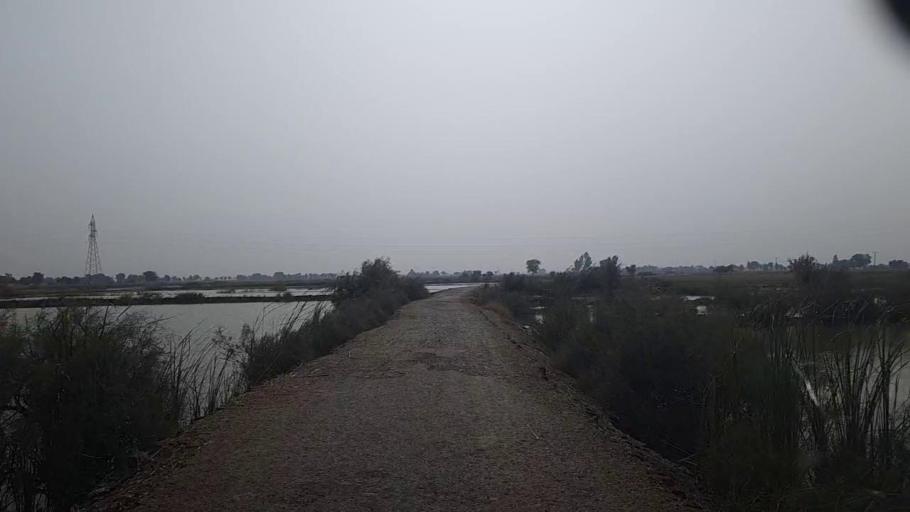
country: PK
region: Sindh
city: Kashmor
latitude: 28.3950
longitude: 69.4213
